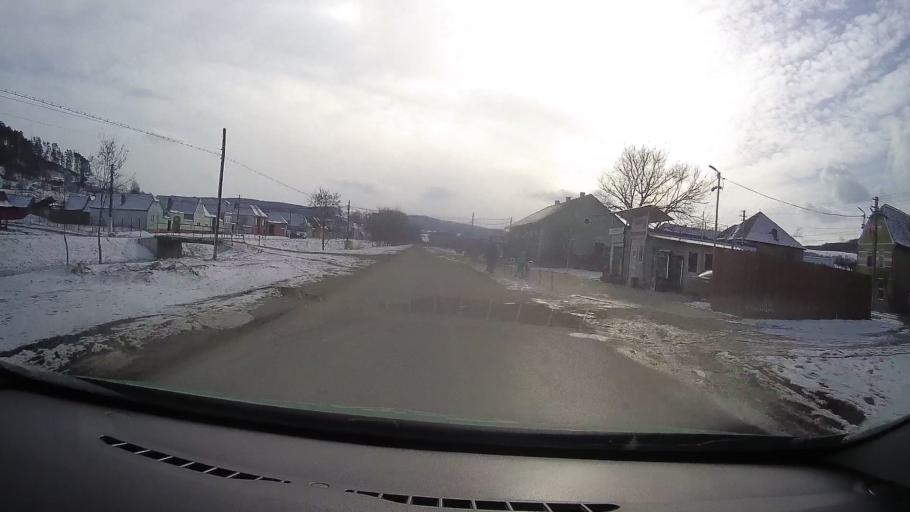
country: RO
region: Sibiu
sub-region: Comuna Bradeni
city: Bradeni
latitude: 46.0823
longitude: 24.8301
